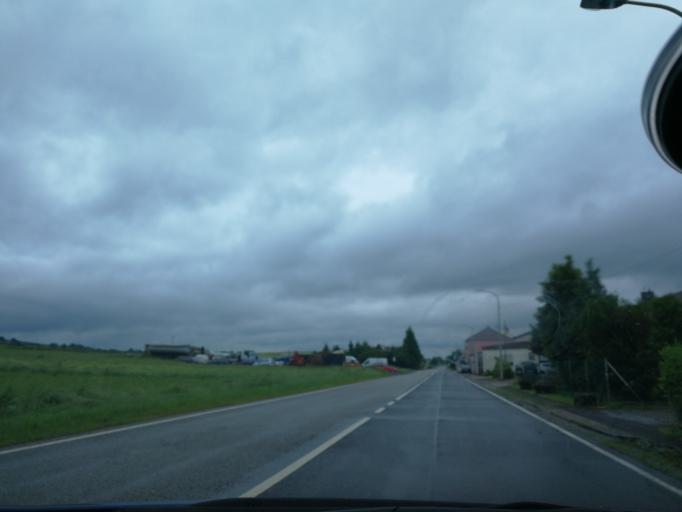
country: DE
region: Rheinland-Pfalz
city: Borrstadt
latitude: 49.5834
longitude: 7.9401
